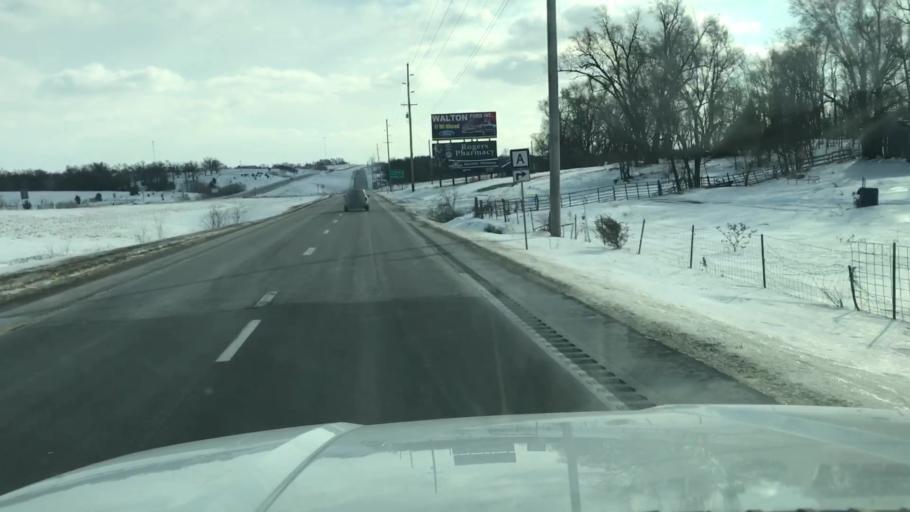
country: US
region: Missouri
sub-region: Nodaway County
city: Maryville
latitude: 40.2027
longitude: -94.8682
